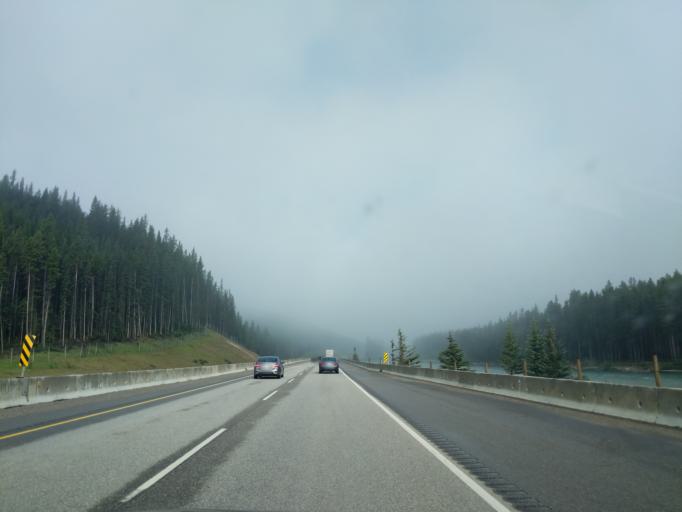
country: CA
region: Alberta
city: Lake Louise
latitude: 51.2847
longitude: -115.9831
